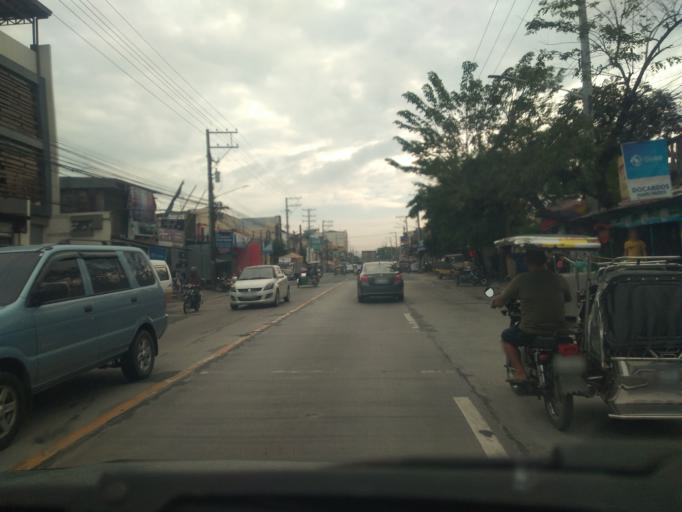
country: PH
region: Central Luzon
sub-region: Province of Pampanga
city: San Fernando
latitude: 15.0332
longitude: 120.6897
